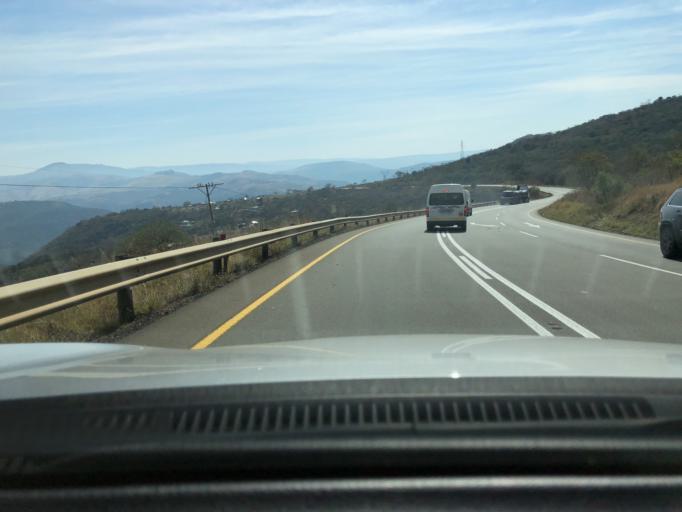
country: ZA
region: KwaZulu-Natal
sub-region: uMgungundlovu District Municipality
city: Richmond
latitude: -30.0352
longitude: 30.2195
